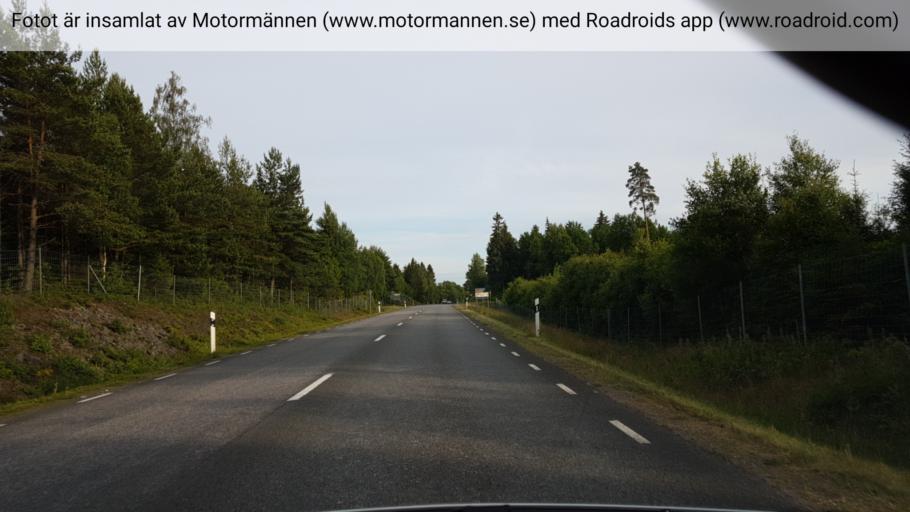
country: SE
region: Vaestra Goetaland
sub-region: Skara Kommun
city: Skara
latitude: 58.3426
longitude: 13.4347
